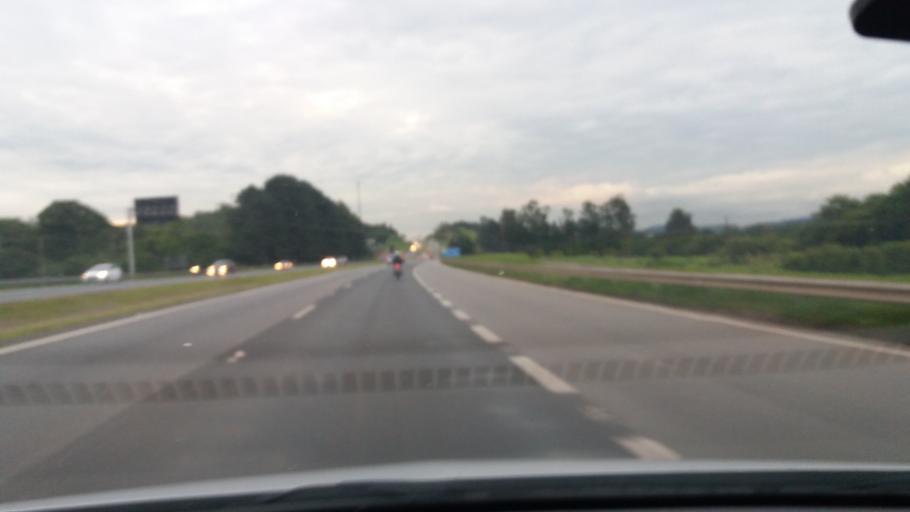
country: BR
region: Sao Paulo
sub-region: Bom Jesus Dos Perdoes
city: Bom Jesus dos Perdoes
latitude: -23.1145
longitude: -46.4877
